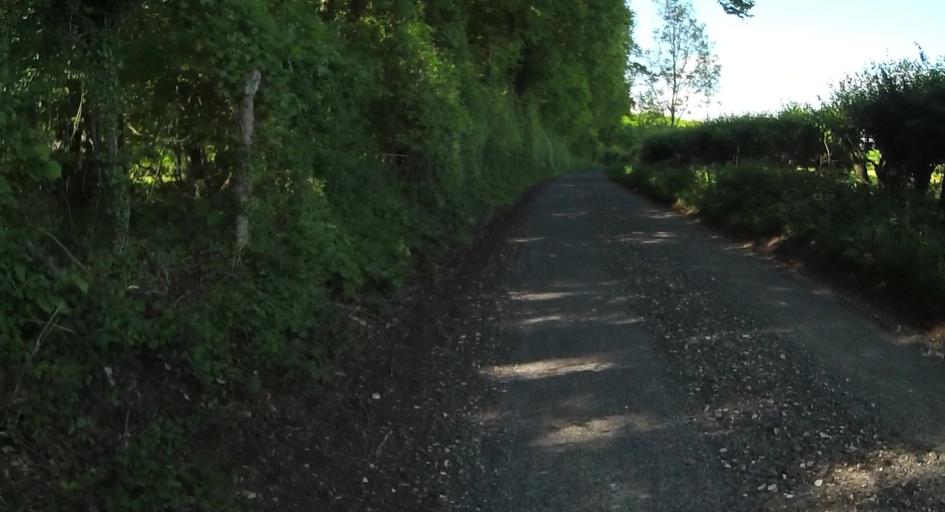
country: GB
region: England
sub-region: Hampshire
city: Overton
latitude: 51.1689
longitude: -1.2194
